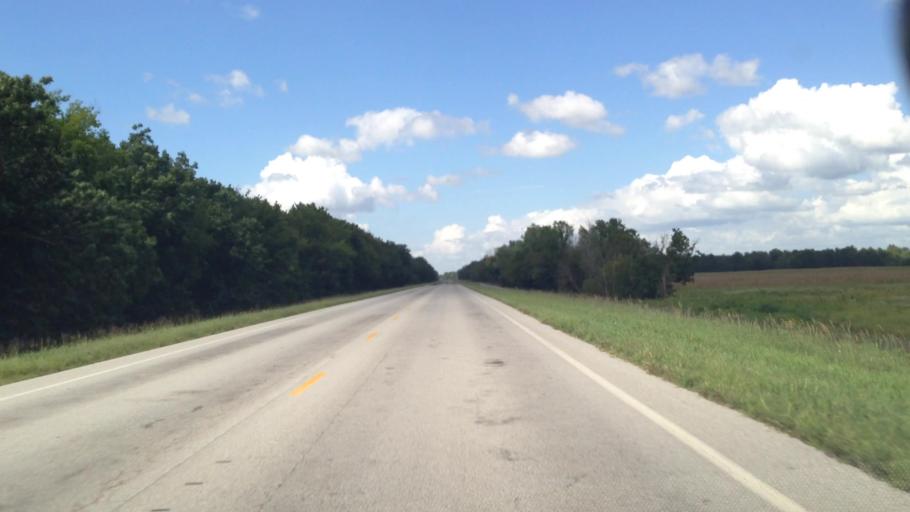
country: US
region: Kansas
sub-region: Labette County
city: Chetopa
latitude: 37.0653
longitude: -95.1033
